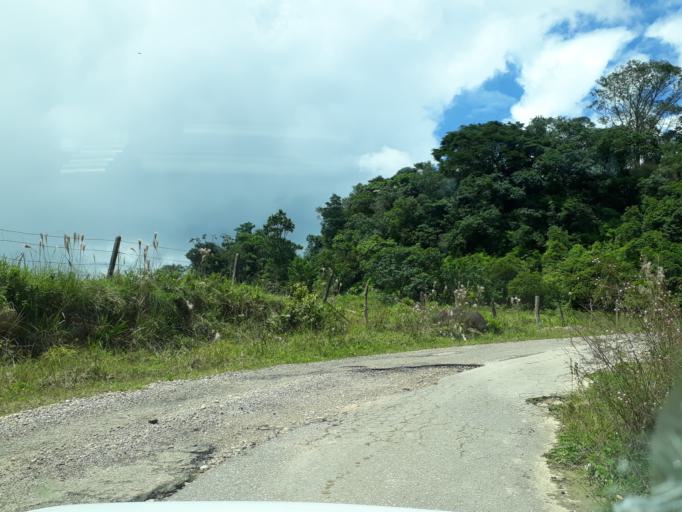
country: CO
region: Cundinamarca
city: Medina
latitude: 4.5817
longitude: -73.3446
